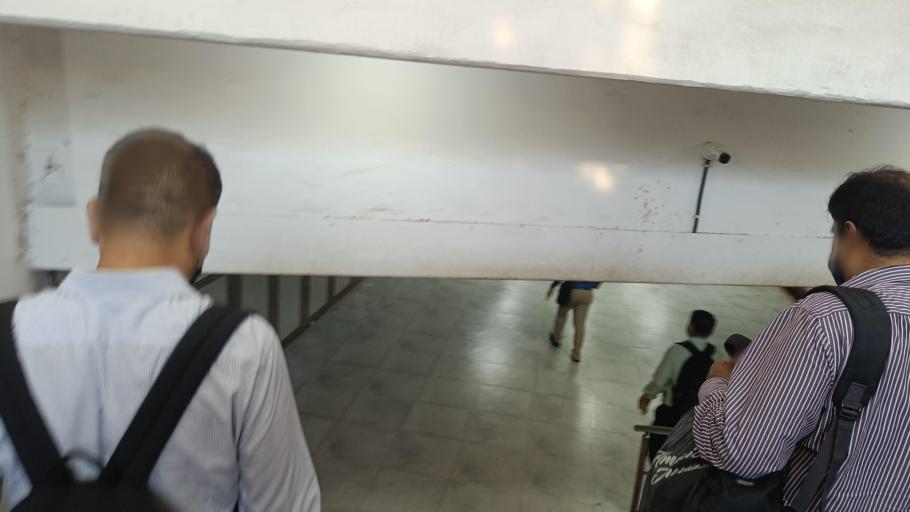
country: IN
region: Maharashtra
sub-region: Raigarh
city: Uran
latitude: 18.9330
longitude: 72.8284
